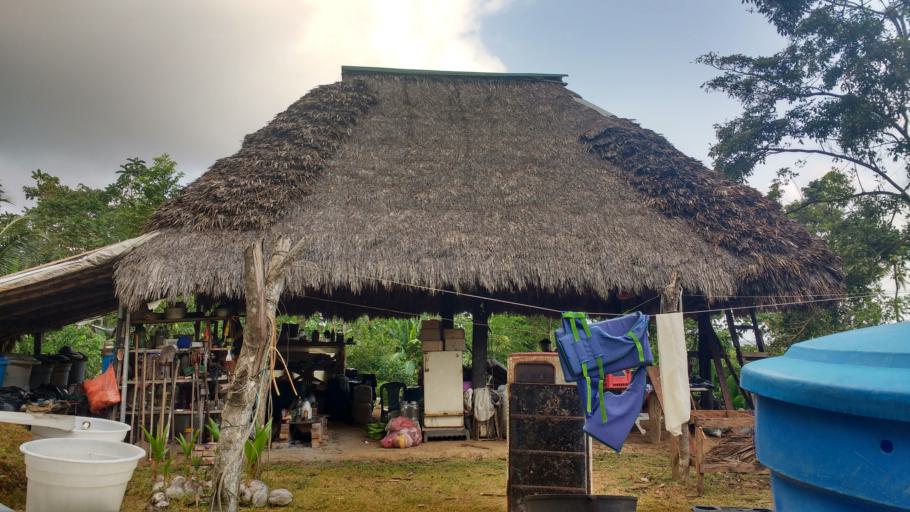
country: CO
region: Choco
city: Acandi
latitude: 8.5715
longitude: -77.2949
